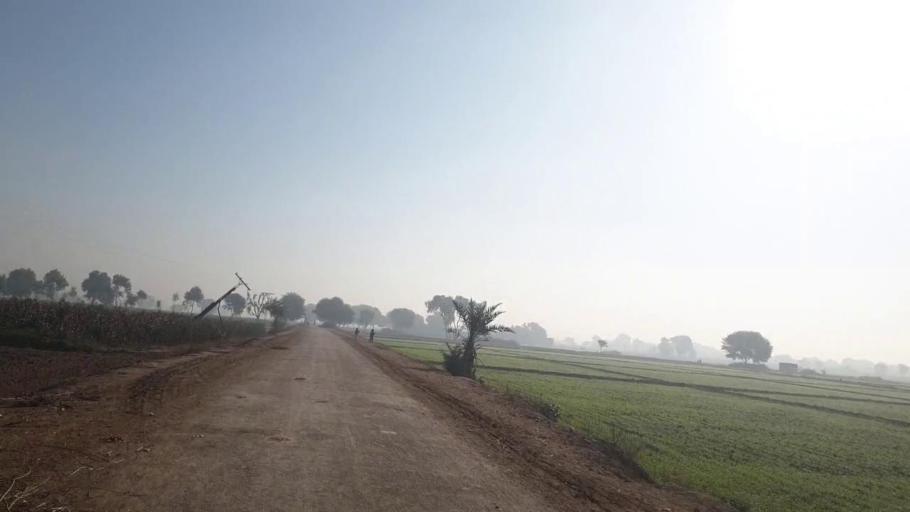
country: PK
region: Sindh
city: Dadu
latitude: 26.6756
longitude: 67.7884
